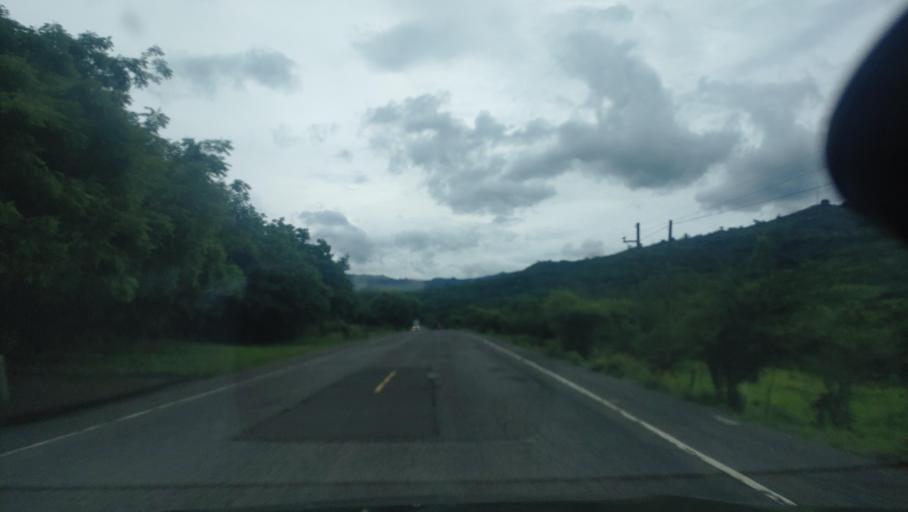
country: HN
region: Choluteca
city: Santa Ana de Yusguare
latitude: 13.3642
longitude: -87.0846
